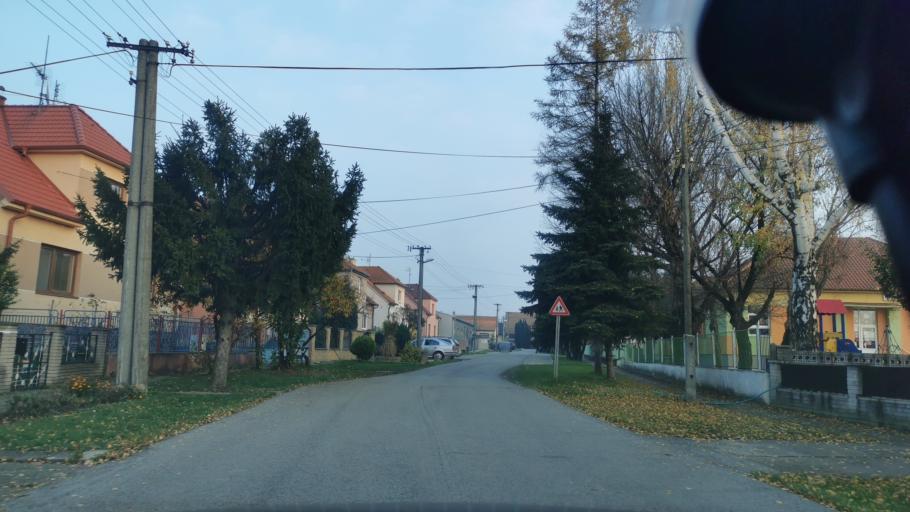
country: SK
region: Trnavsky
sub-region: Okres Skalica
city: Holic
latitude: 48.8264
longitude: 17.1924
